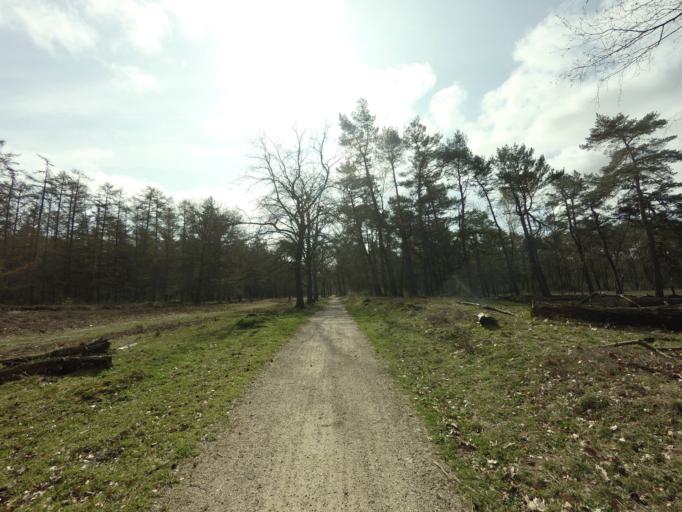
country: NL
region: North Holland
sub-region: Gemeente Hilversum
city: Hilversum
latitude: 52.1928
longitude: 5.1942
